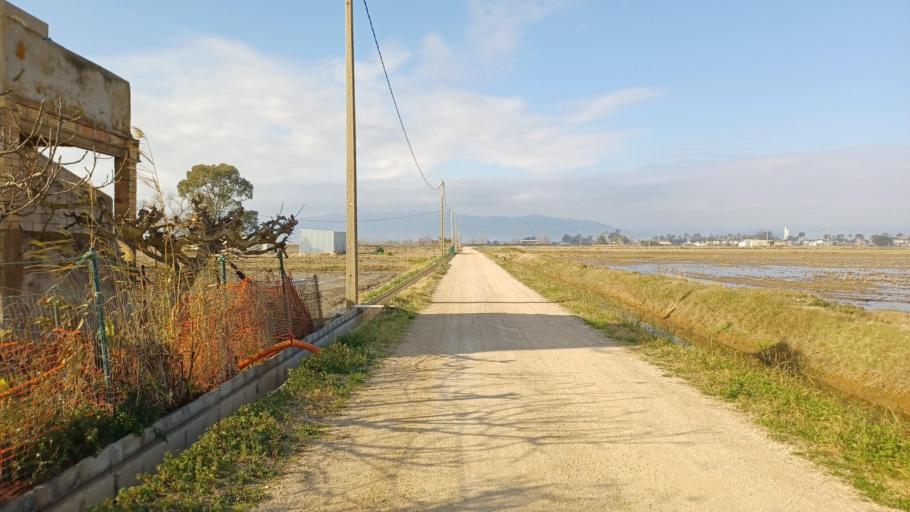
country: ES
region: Catalonia
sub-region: Provincia de Tarragona
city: Deltebre
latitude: 40.6422
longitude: 0.6977
